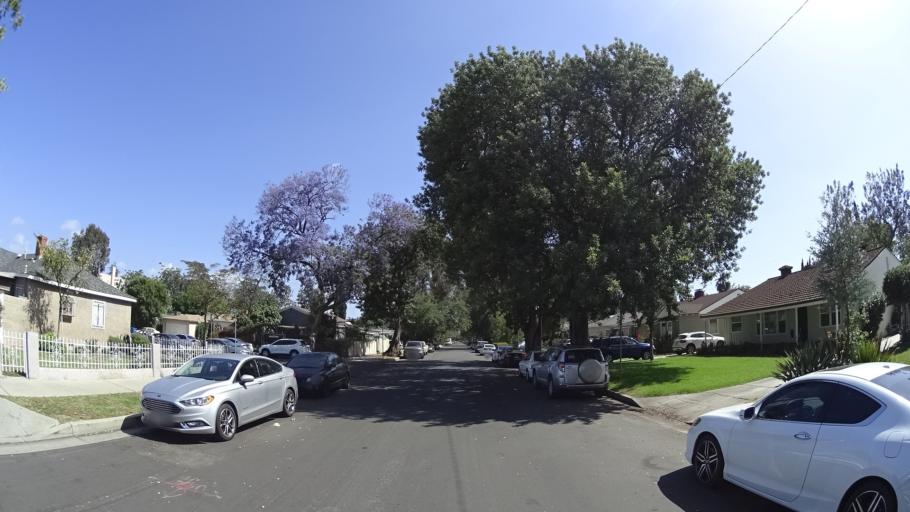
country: US
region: California
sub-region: Los Angeles County
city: North Hollywood
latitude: 34.1770
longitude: -118.3834
